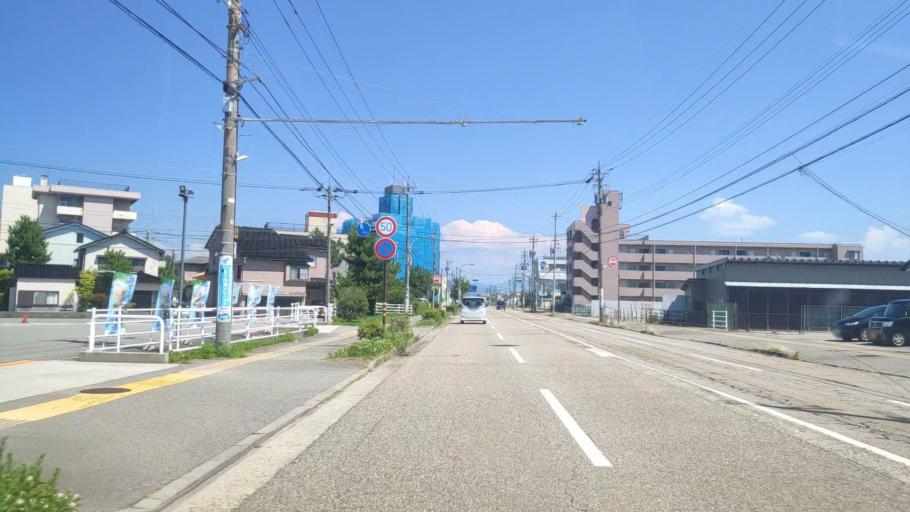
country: JP
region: Ishikawa
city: Kanazawa-shi
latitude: 36.6003
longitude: 136.5955
